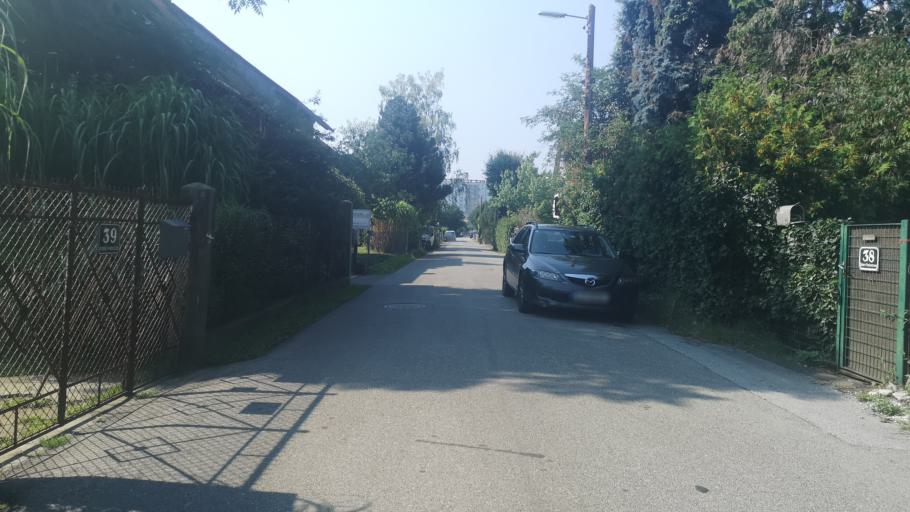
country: AT
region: Styria
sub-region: Graz Stadt
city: Wetzelsdorf
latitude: 47.0448
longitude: 15.4134
